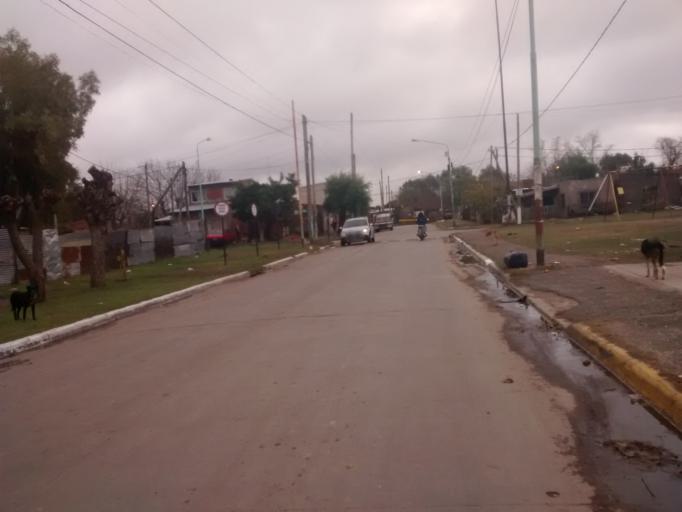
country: AR
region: Buenos Aires
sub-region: Partido de La Plata
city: La Plata
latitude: -34.8899
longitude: -57.9431
